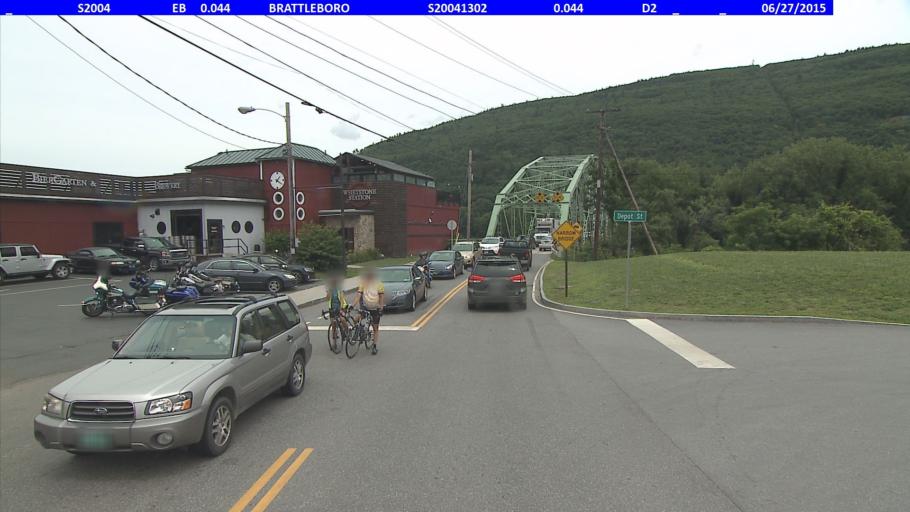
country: US
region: Vermont
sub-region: Windham County
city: Brattleboro
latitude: 42.8513
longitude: -72.5565
